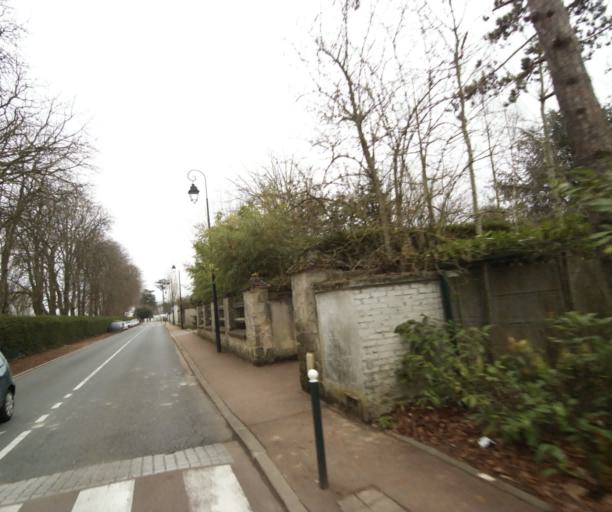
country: FR
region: Ile-de-France
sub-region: Departement des Hauts-de-Seine
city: Garches
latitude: 48.8481
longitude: 2.1744
